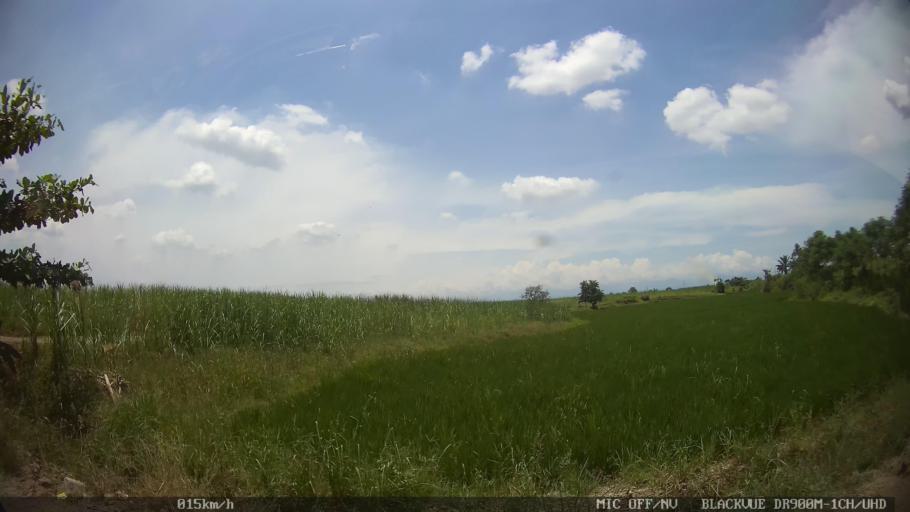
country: ID
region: North Sumatra
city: Binjai
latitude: 3.5912
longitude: 98.5288
